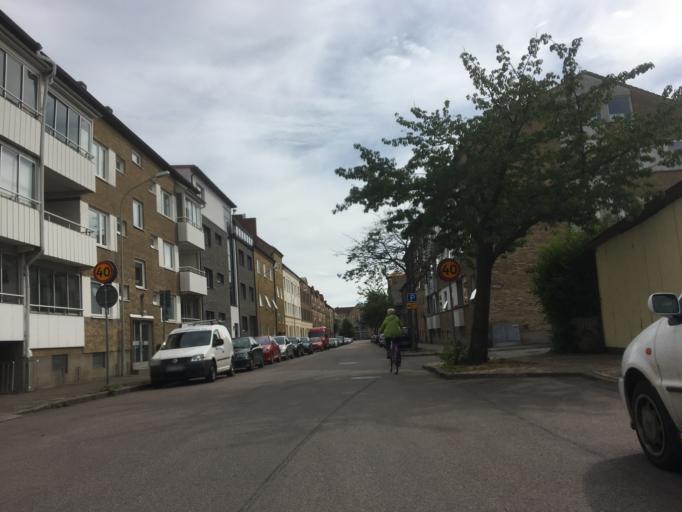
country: SE
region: Skane
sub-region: Landskrona
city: Landskrona
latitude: 55.8783
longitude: 12.8309
